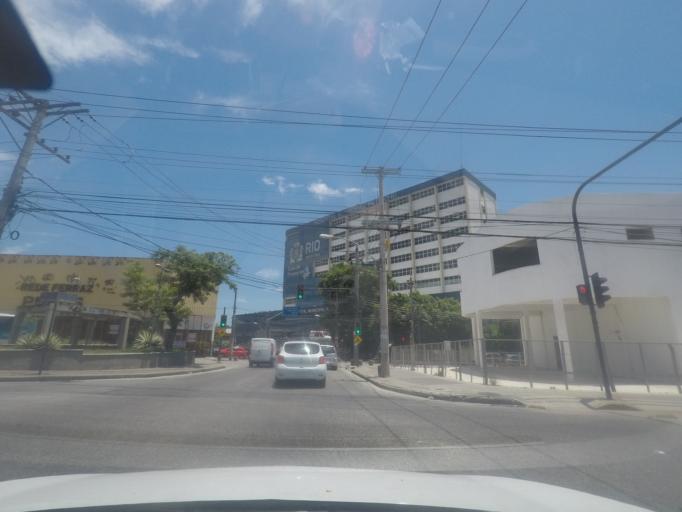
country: BR
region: Rio de Janeiro
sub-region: Itaguai
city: Itaguai
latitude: -22.9119
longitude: -43.6875
